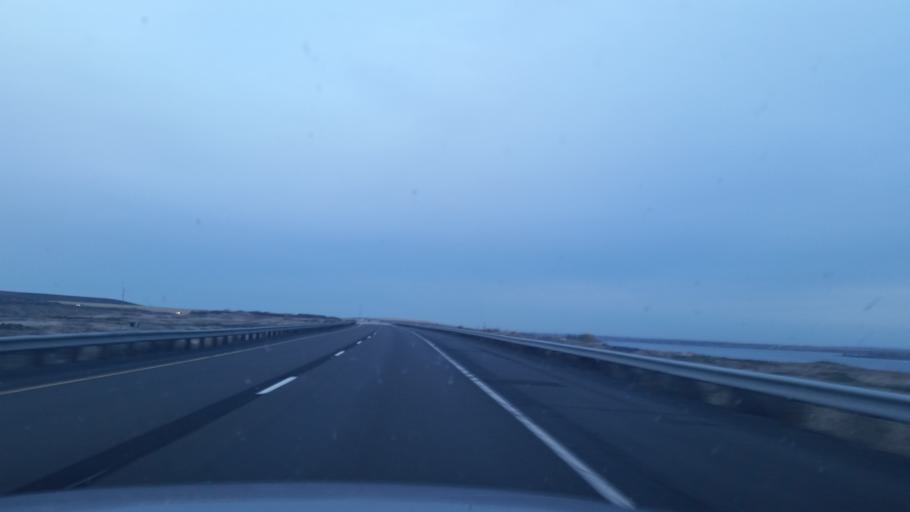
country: US
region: Washington
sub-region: Adams County
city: Ritzville
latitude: 47.2468
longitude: -118.1093
